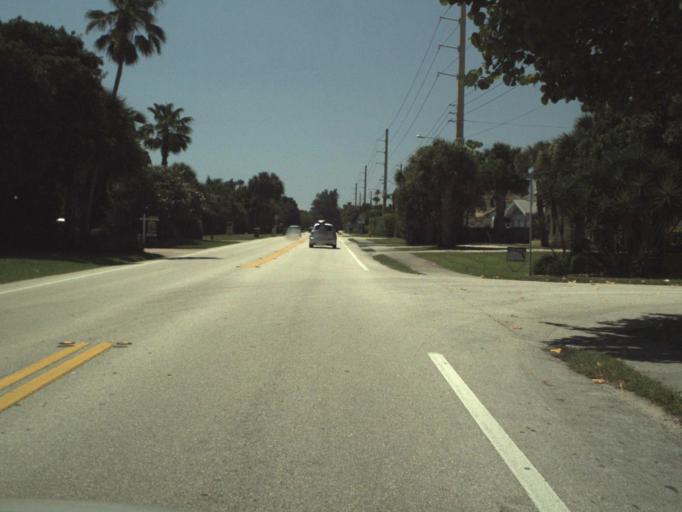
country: US
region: Florida
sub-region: Brevard County
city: Indialantic
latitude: 28.0800
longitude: -80.5624
